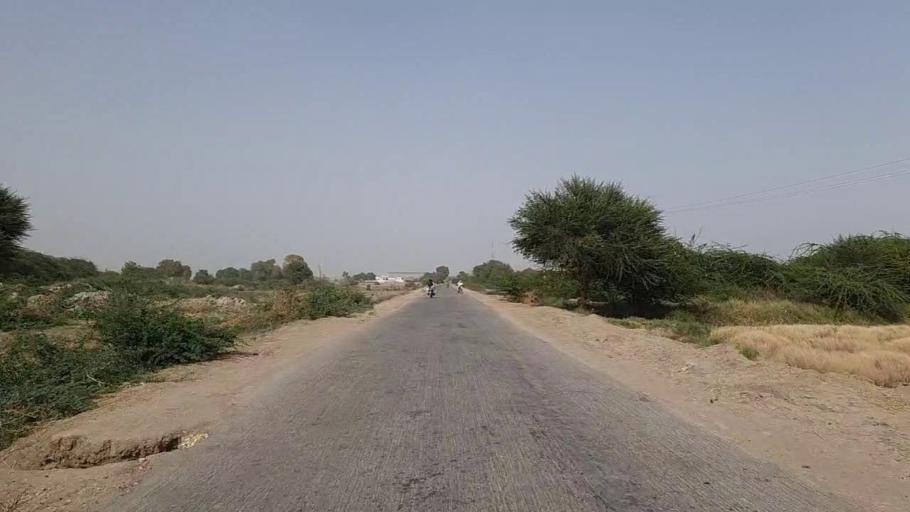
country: PK
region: Sindh
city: Tando Bago
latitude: 24.9190
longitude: 69.1017
